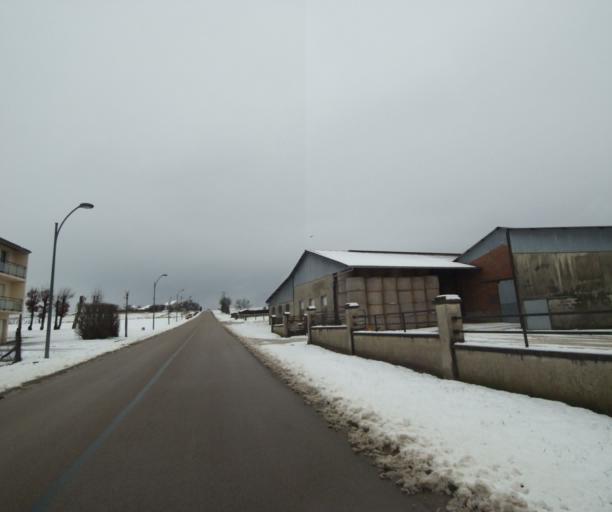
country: FR
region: Champagne-Ardenne
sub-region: Departement de la Haute-Marne
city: Laneuville-a-Remy
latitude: 48.4173
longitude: 4.8378
